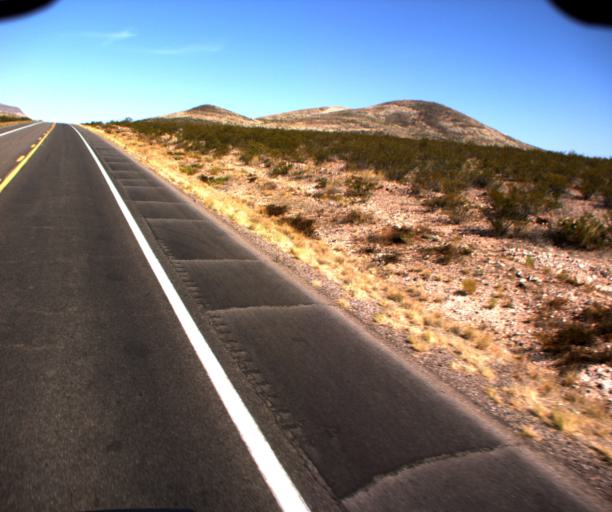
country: US
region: Arizona
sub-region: Greenlee County
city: Clifton
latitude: 32.7275
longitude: -109.1785
